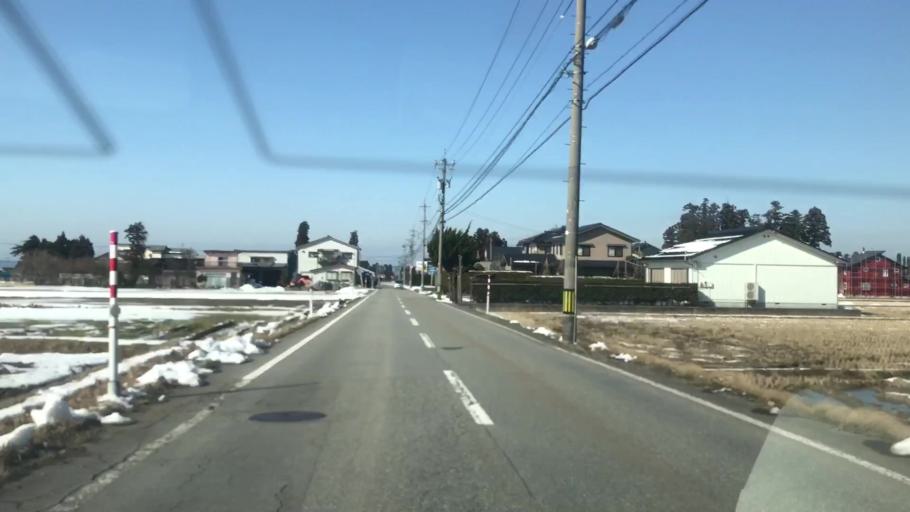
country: JP
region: Toyama
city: Toyama-shi
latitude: 36.6257
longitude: 137.2775
